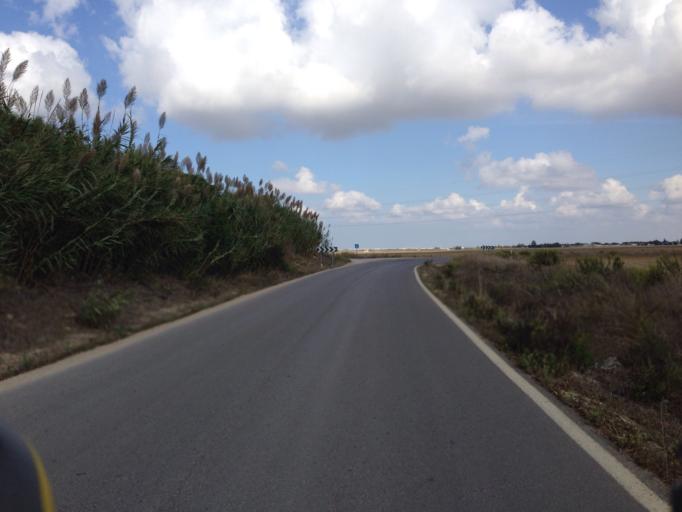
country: ES
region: Andalusia
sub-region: Provincia de Cadiz
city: Conil de la Frontera
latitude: 36.3504
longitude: -6.0620
